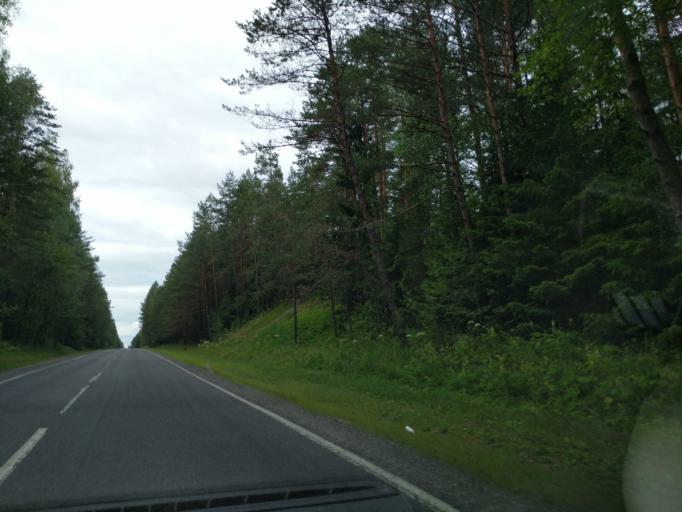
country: BY
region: Minsk
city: Myadzyel
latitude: 54.7949
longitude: 27.0157
